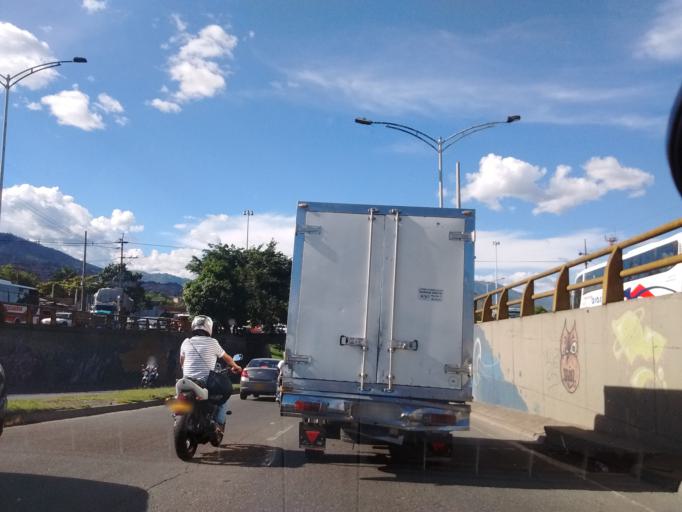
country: CO
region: Antioquia
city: Medellin
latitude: 6.2750
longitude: -75.5728
